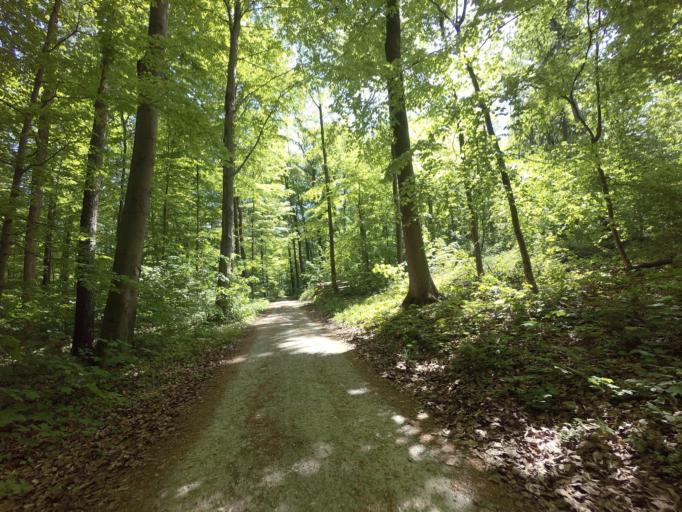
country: DE
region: Lower Saxony
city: Hildesheim
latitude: 52.1372
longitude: 9.9908
